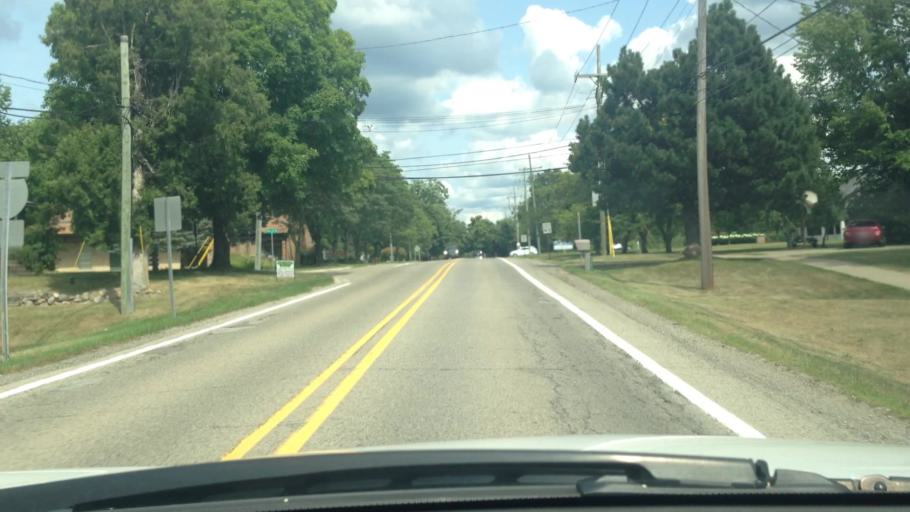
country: US
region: Michigan
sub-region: Oakland County
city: Clarkston
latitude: 42.7401
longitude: -83.4101
